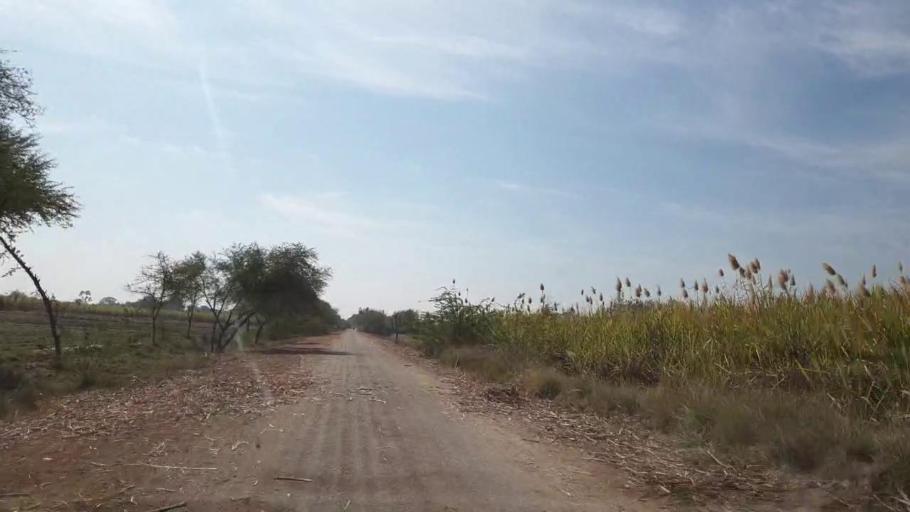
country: PK
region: Sindh
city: Mirpur Khas
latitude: 25.5262
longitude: 69.1452
